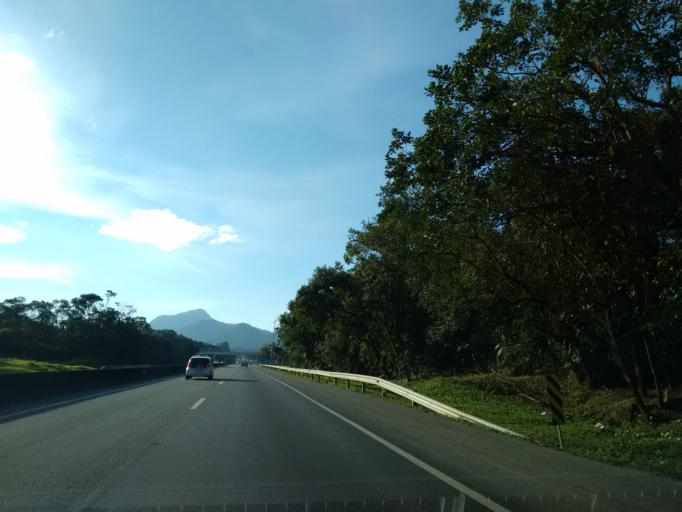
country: BR
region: Santa Catarina
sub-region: Joinville
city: Joinville
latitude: -26.0549
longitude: -48.8595
